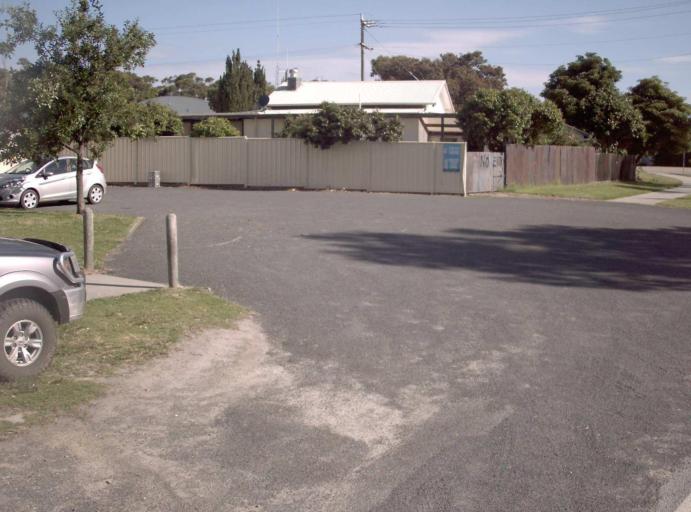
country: AU
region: Victoria
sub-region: East Gippsland
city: Lakes Entrance
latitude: -37.7955
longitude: 148.5329
